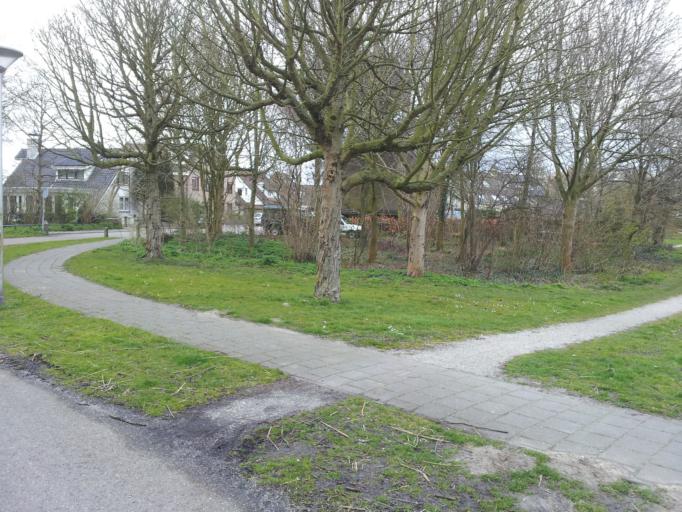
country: NL
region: South Holland
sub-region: Gemeente Wassenaar
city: Wassenaar
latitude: 52.1523
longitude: 4.4072
